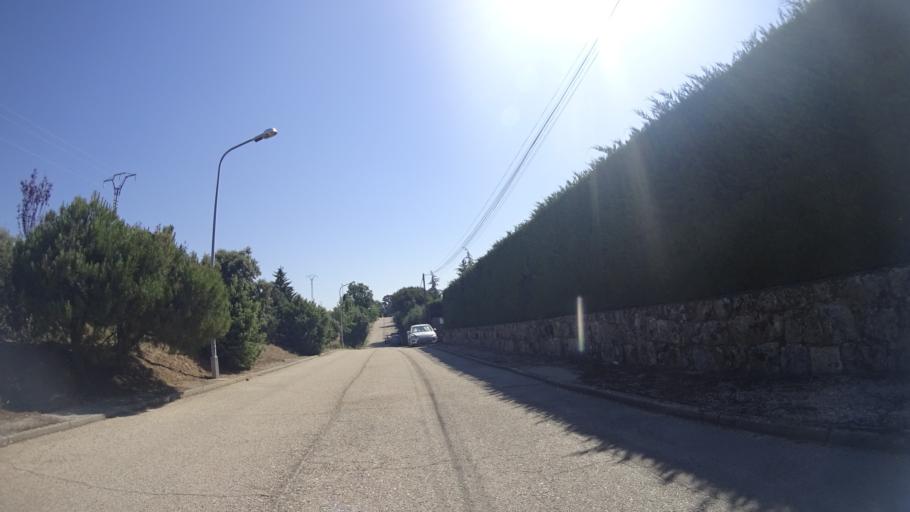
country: ES
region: Madrid
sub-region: Provincia de Madrid
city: Hoyo de Manzanares
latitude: 40.6044
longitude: -3.9062
